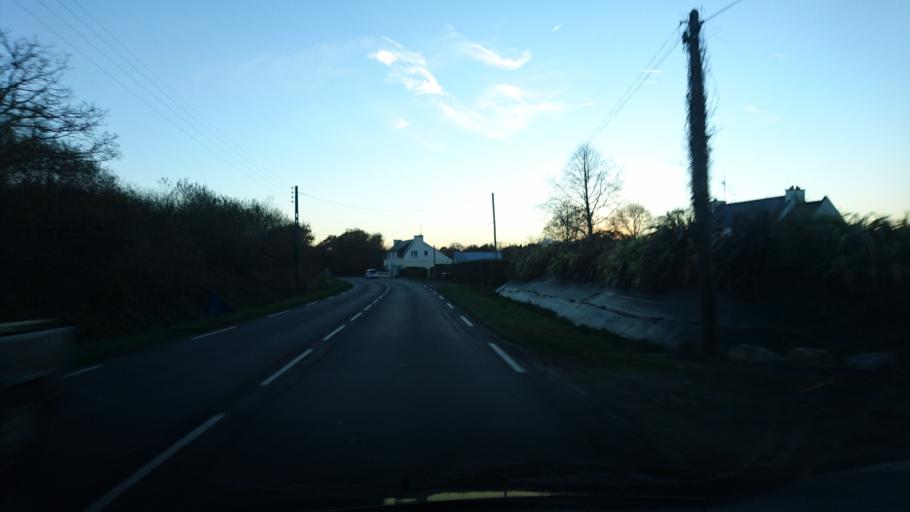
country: FR
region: Brittany
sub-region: Departement du Finistere
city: Quimperle
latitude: 47.8553
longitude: -3.5683
